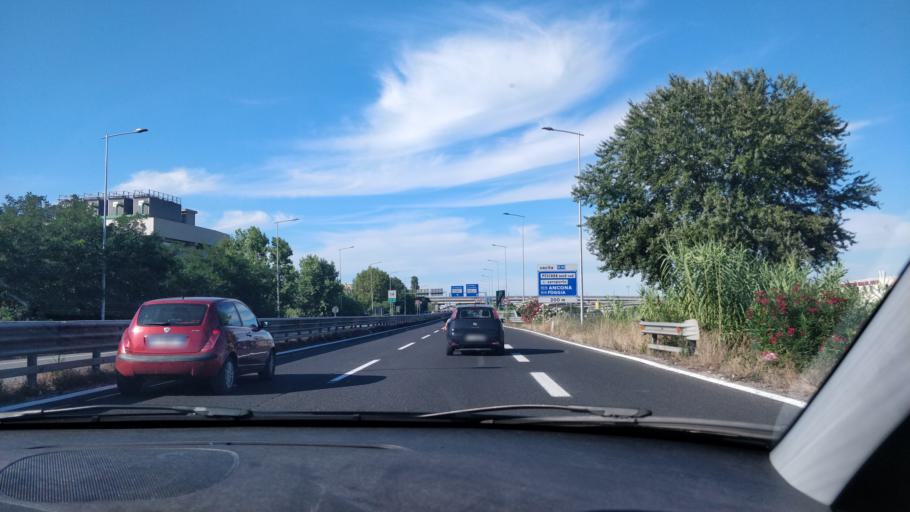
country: IT
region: Abruzzo
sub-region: Provincia di Pescara
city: Villa Raspa
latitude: 42.4415
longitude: 14.1863
